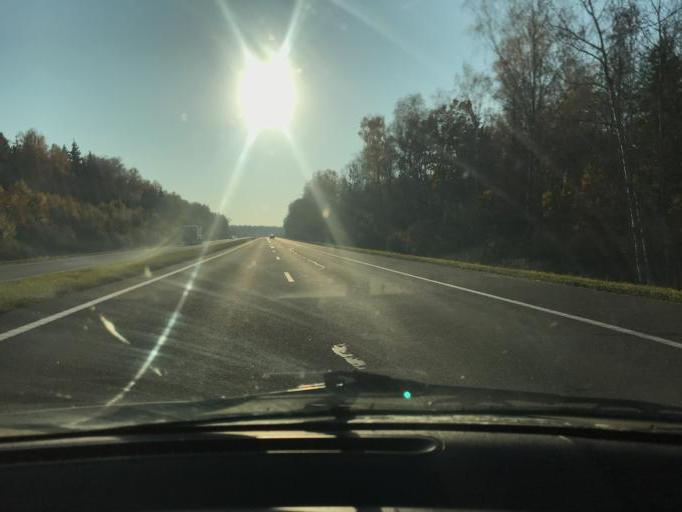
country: BY
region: Minsk
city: Loshnitsa
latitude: 54.2769
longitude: 28.7268
